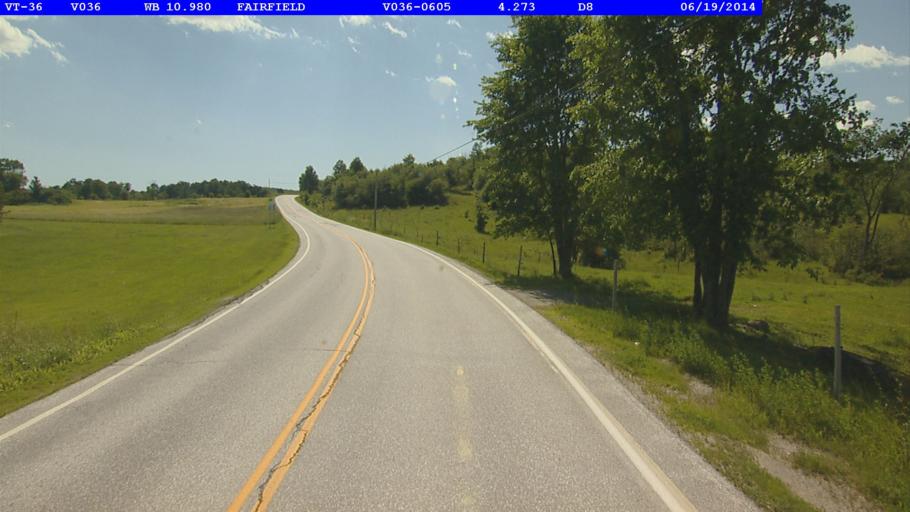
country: US
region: Vermont
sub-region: Franklin County
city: Saint Albans
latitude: 44.8013
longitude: -72.9494
